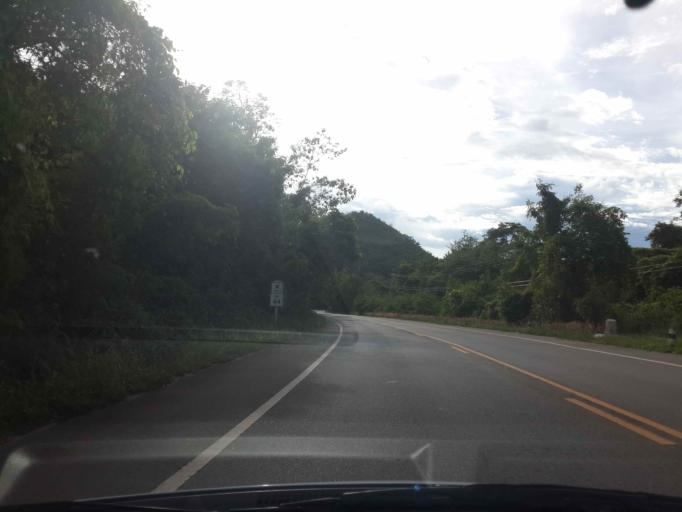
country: TH
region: Kanchanaburi
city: Sai Yok
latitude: 13.9279
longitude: 99.1193
